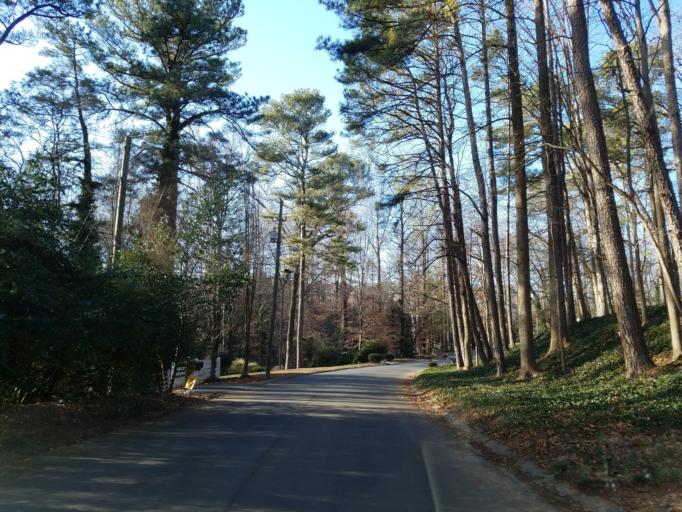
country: US
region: Georgia
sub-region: Cobb County
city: Vinings
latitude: 33.8544
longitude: -84.4868
